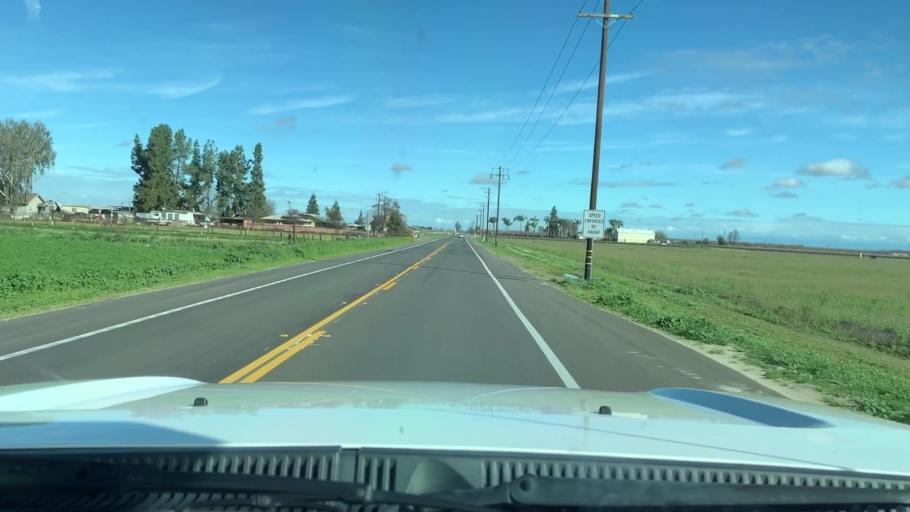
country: US
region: California
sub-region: Fresno County
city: Laton
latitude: 36.4909
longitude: -119.6829
